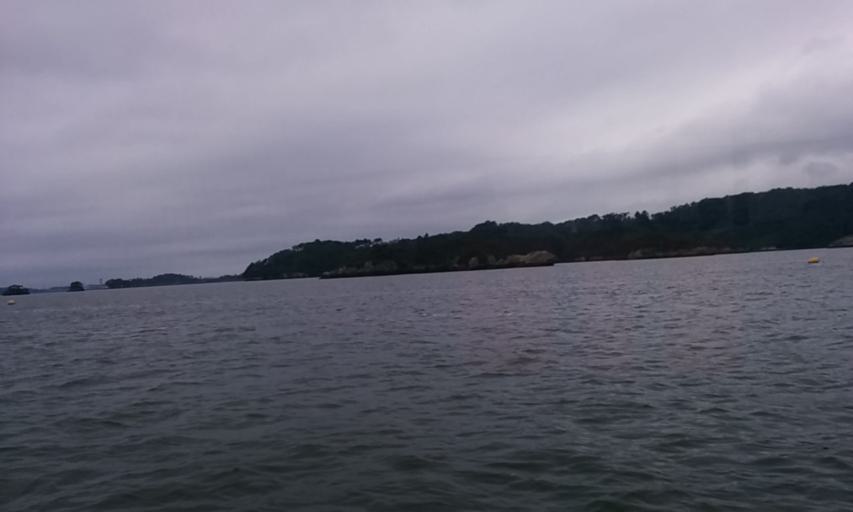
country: JP
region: Miyagi
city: Matsushima
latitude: 38.3573
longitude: 141.0726
